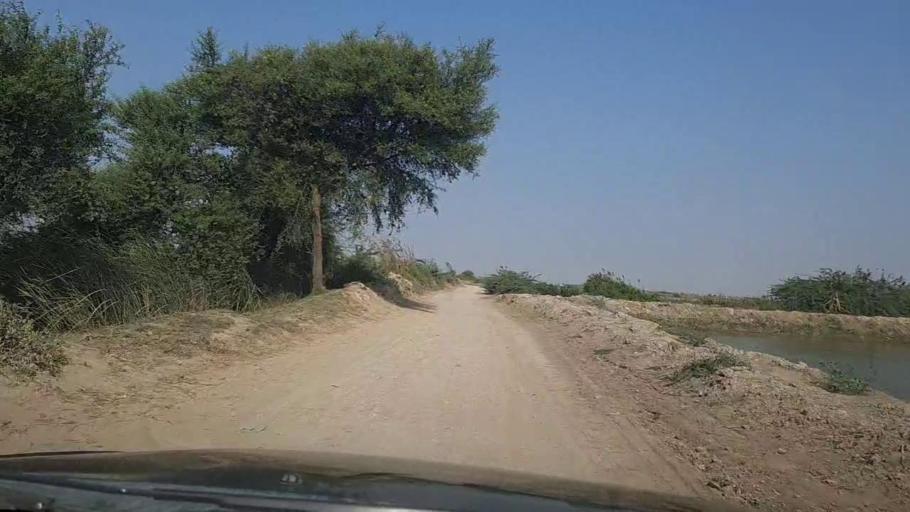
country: PK
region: Sindh
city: Thatta
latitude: 24.6355
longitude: 67.8136
